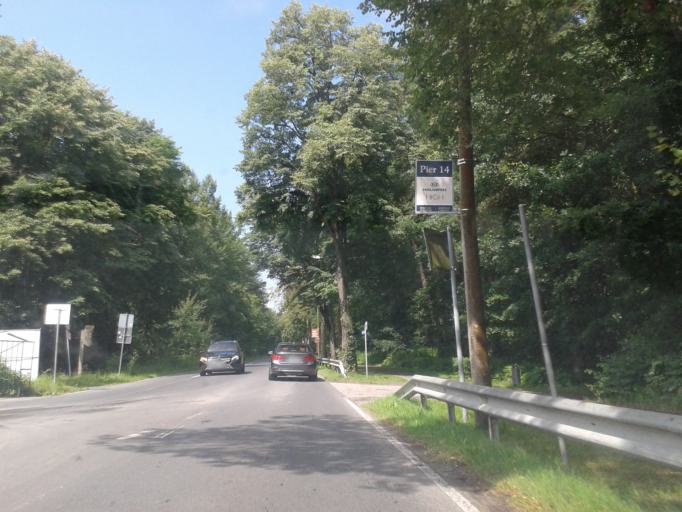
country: PL
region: West Pomeranian Voivodeship
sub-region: Swinoujscie
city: Swinoujscie
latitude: 53.9240
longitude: 14.2130
